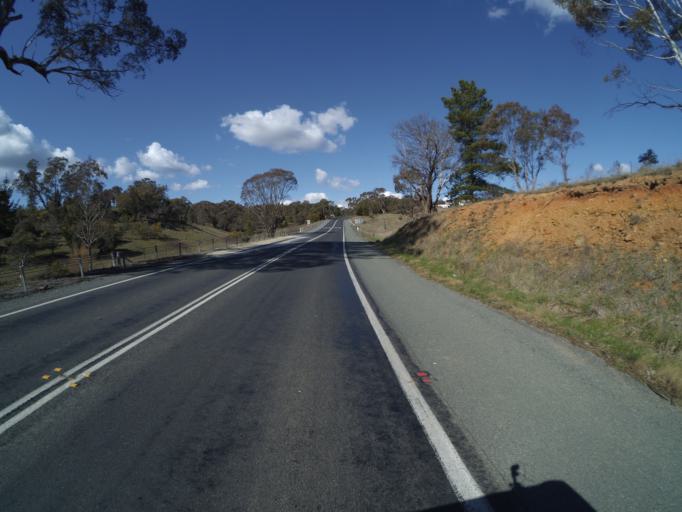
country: AU
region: New South Wales
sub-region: Queanbeyan
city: Queanbeyan
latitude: -35.3369
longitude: 149.2899
